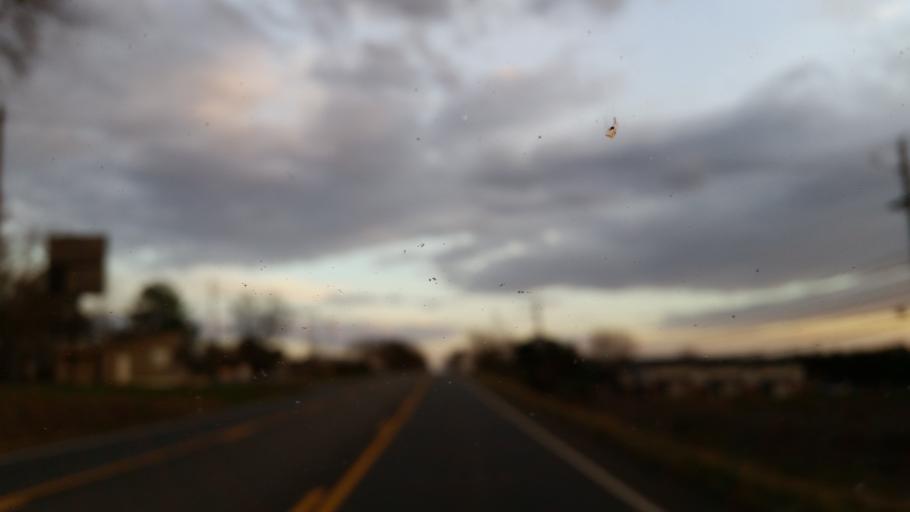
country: US
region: Georgia
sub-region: Pickens County
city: Jasper
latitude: 34.4565
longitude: -84.4099
